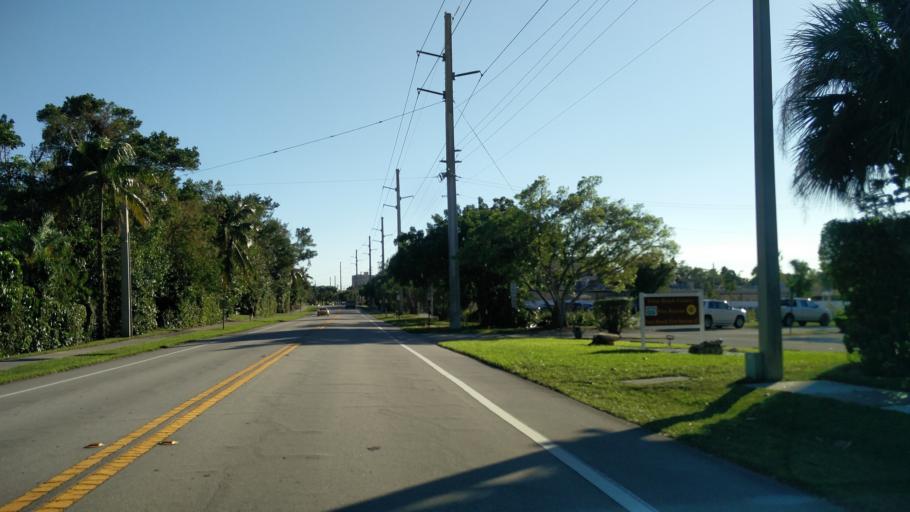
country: US
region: Florida
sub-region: Palm Beach County
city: Juno Beach
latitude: 26.8661
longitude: -80.0537
